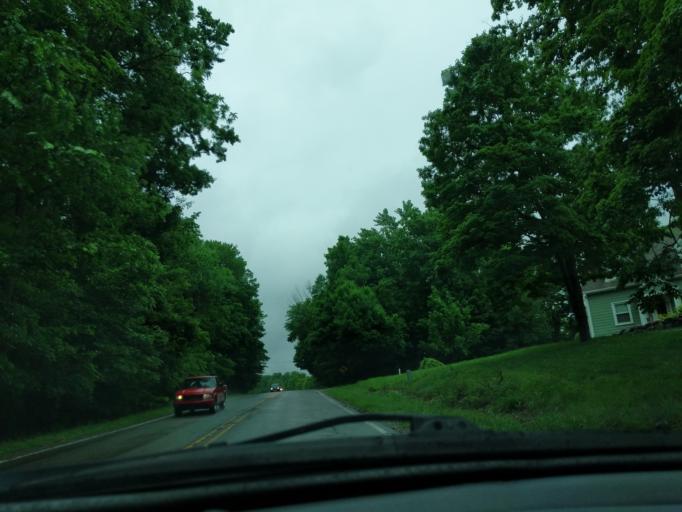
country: US
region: Indiana
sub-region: Hamilton County
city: Noblesville
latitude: 40.0576
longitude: -86.0444
